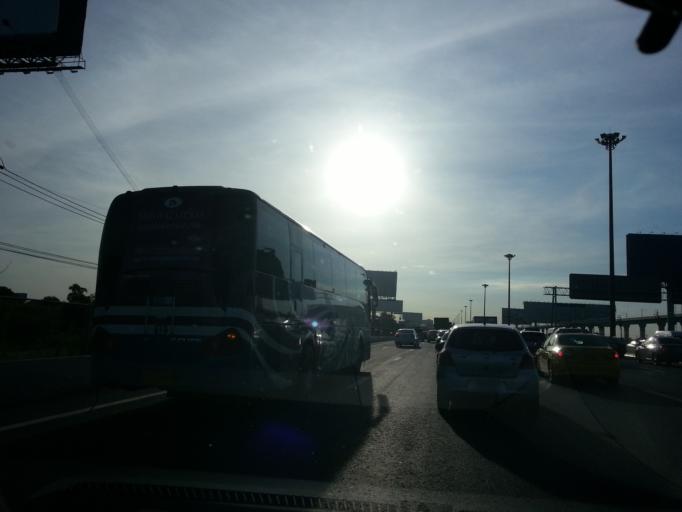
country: TH
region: Bangkok
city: Saphan Sung
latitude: 13.7318
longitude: 100.7116
